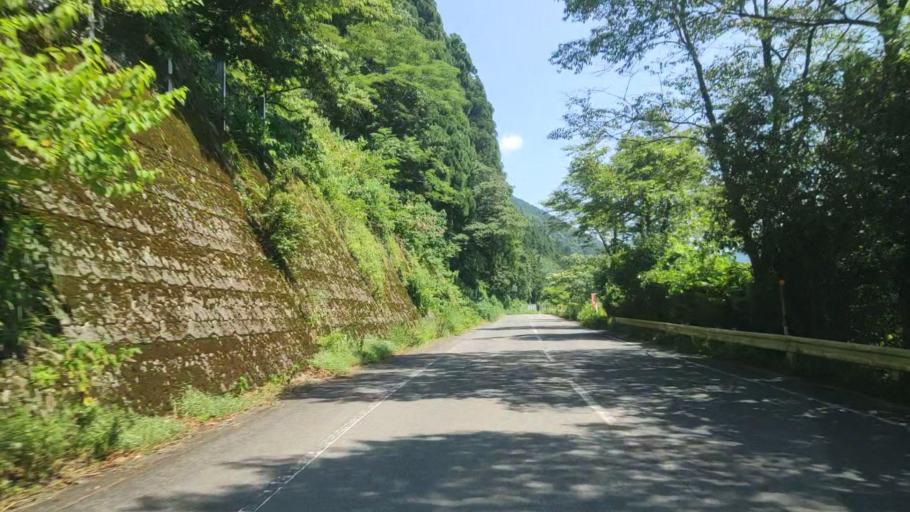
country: JP
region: Gifu
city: Godo
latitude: 35.6105
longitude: 136.6265
